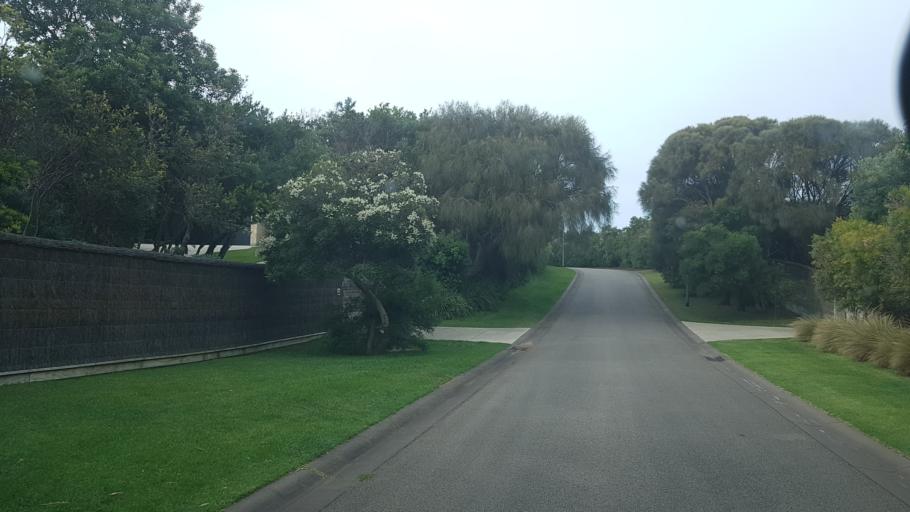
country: AU
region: Victoria
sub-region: Mornington Peninsula
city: Sorrento
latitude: -38.3332
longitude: 144.7131
